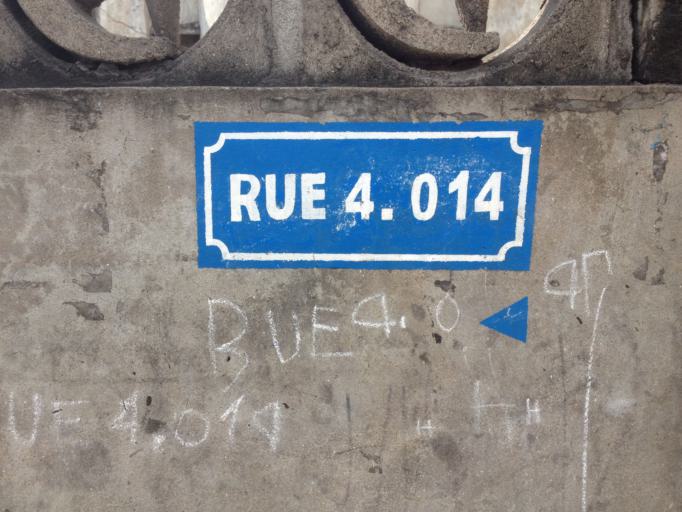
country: BJ
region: Littoral
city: Cotonou
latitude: 6.3593
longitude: 2.4481
